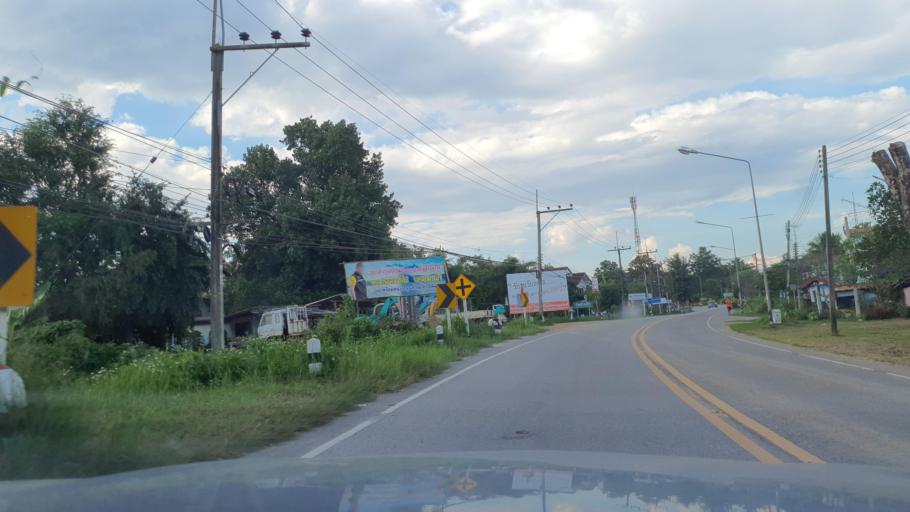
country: TH
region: Phayao
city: Phayao
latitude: 19.1308
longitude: 99.8416
